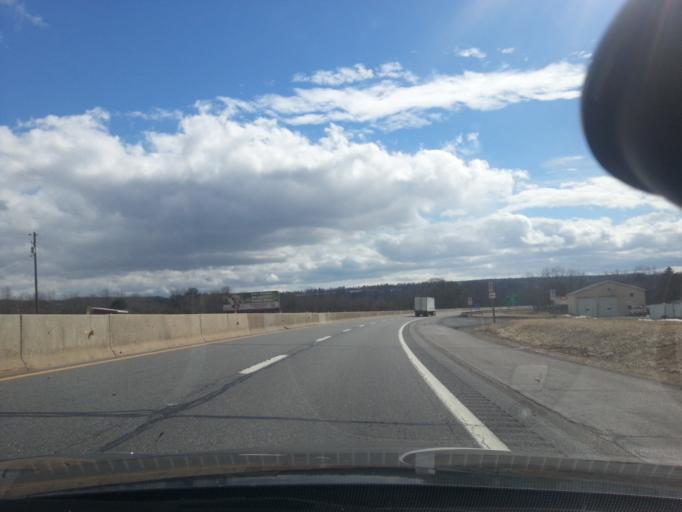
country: US
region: Pennsylvania
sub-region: Carbon County
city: Weissport East
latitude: 40.8614
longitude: -75.6502
